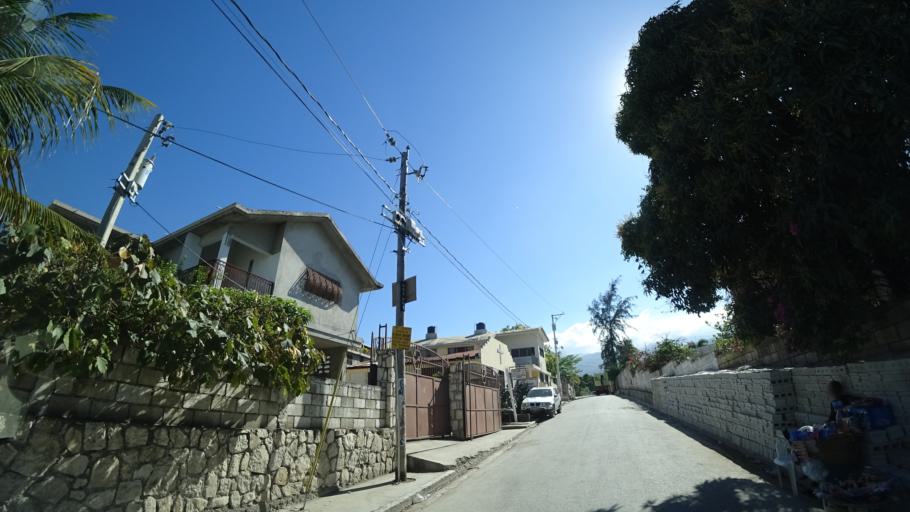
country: HT
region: Ouest
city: Delmas 73
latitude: 18.5417
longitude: -72.2867
